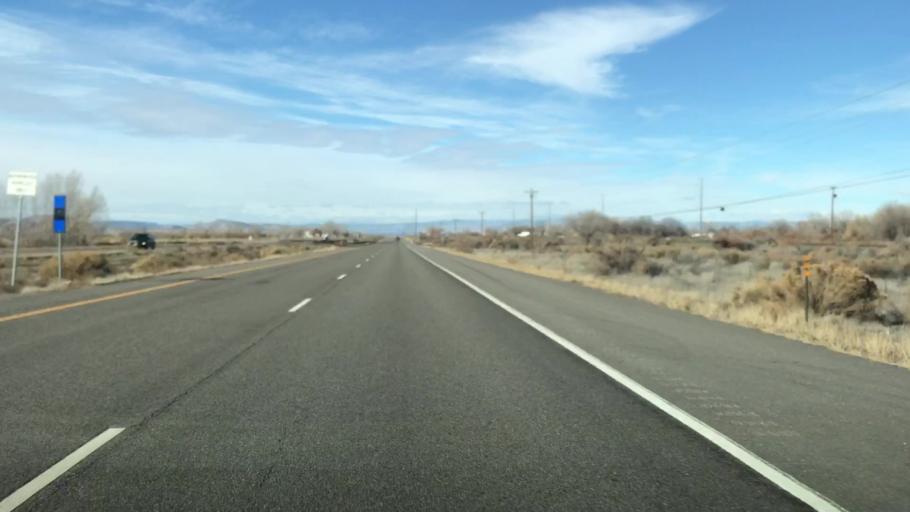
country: US
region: Colorado
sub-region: Mesa County
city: Fruita
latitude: 39.1347
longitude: -108.6951
